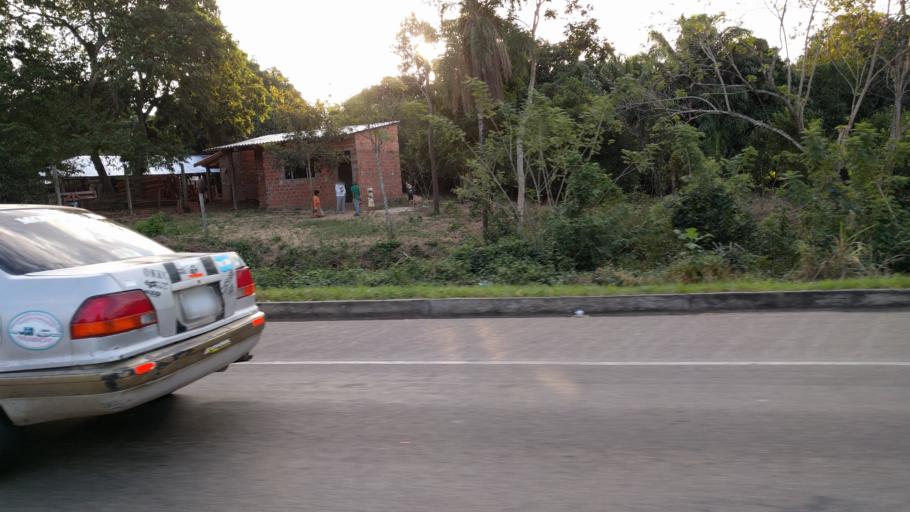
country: BO
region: Santa Cruz
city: Buena Vista
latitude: -17.4144
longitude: -63.6169
